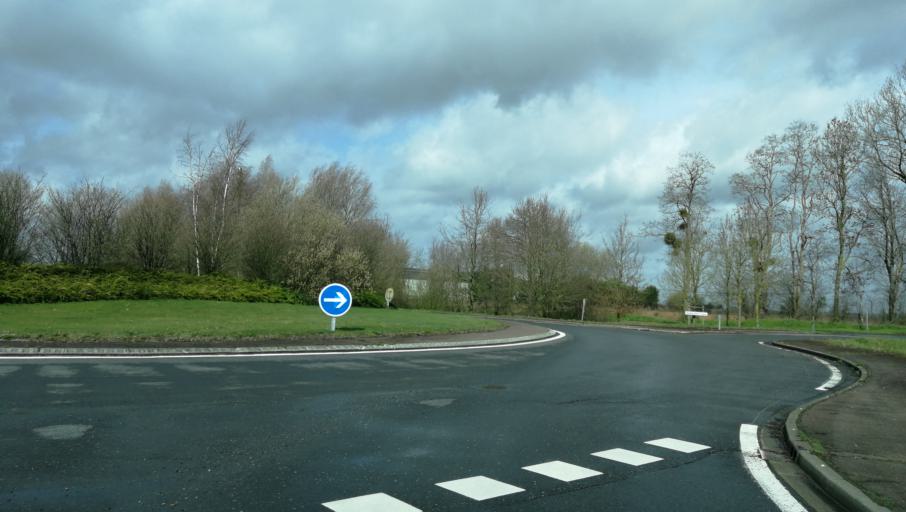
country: FR
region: Haute-Normandie
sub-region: Departement de l'Eure
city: Beuzeville
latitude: 49.3189
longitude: 0.3790
